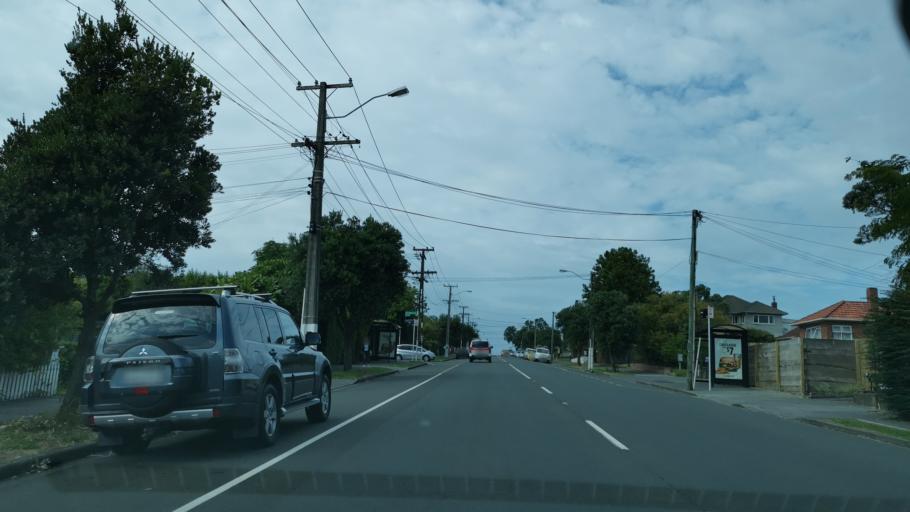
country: NZ
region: Auckland
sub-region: Auckland
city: Rosebank
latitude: -36.8886
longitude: 174.7006
